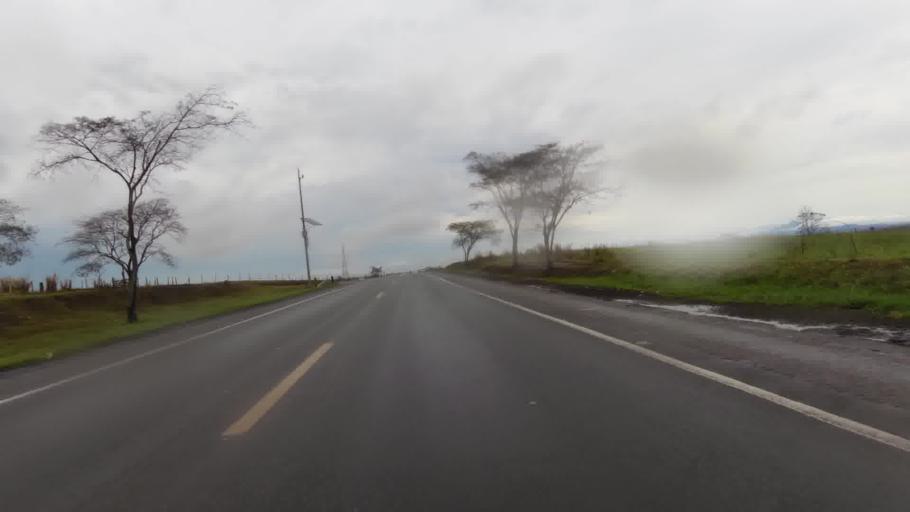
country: BR
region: Rio de Janeiro
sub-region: Campos Dos Goytacazes
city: Campos
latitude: -21.5259
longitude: -41.3372
